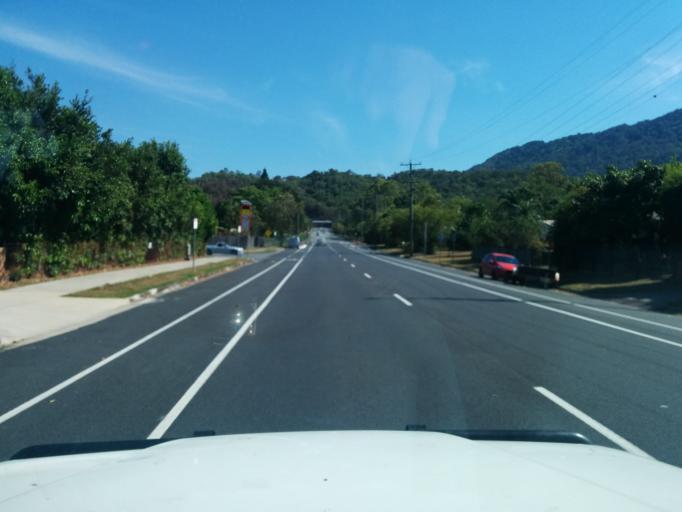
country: AU
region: Queensland
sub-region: Cairns
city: Redlynch
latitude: -16.9092
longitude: 145.7283
